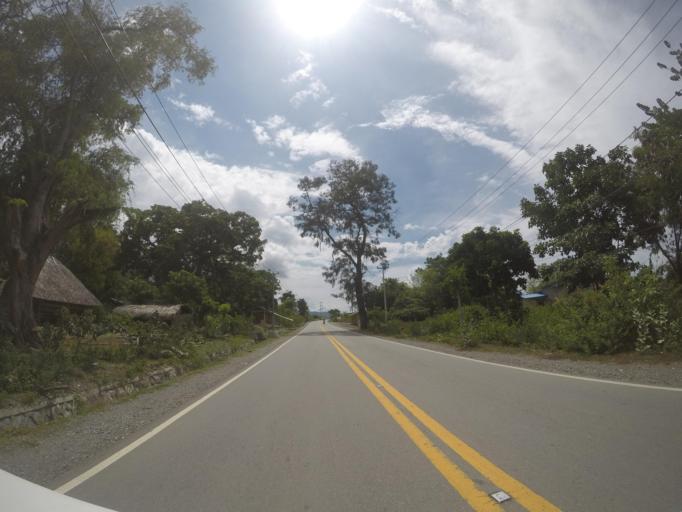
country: TL
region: Liquica
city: Liquica
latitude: -8.5834
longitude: 125.3551
